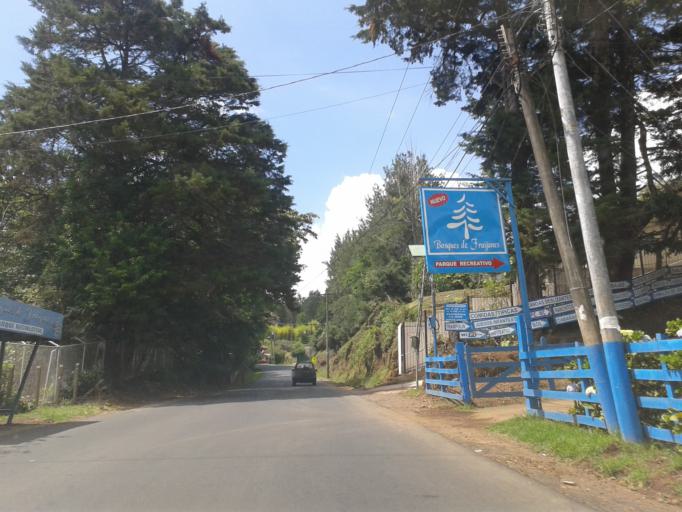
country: CR
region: Alajuela
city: Sabanilla
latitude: 10.1243
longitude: -84.1900
